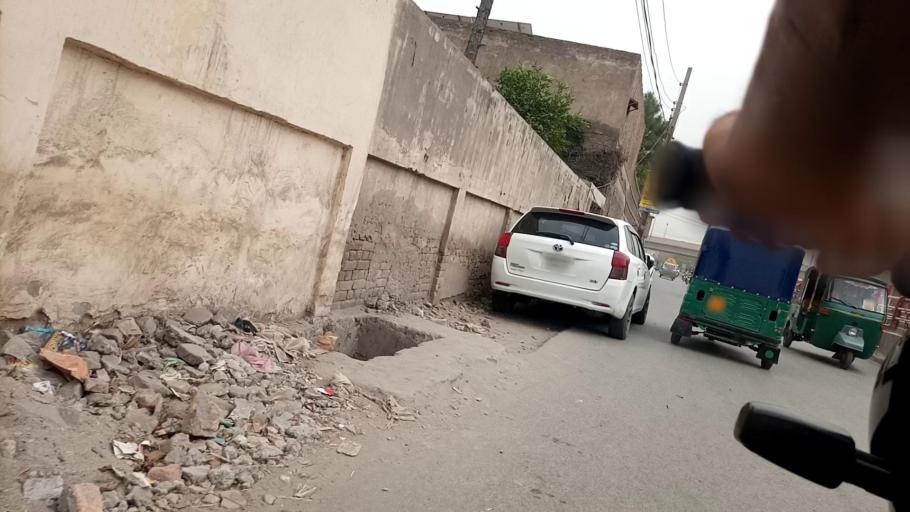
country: PK
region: Khyber Pakhtunkhwa
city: Peshawar
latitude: 34.0172
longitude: 71.5928
